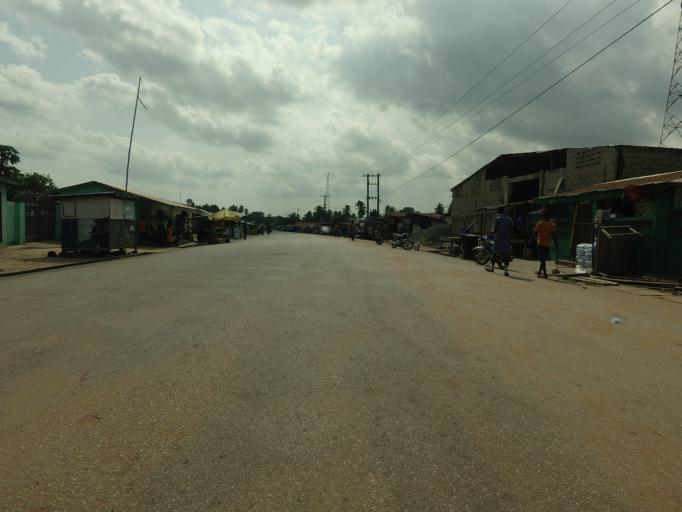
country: GH
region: Volta
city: Ho
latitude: 6.4176
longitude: 0.7437
